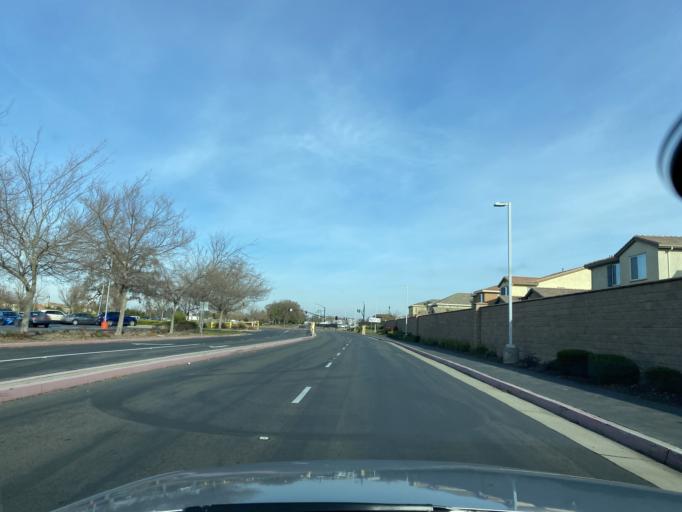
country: US
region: California
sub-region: Sacramento County
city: Elk Grove
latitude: 38.3997
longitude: -121.3946
